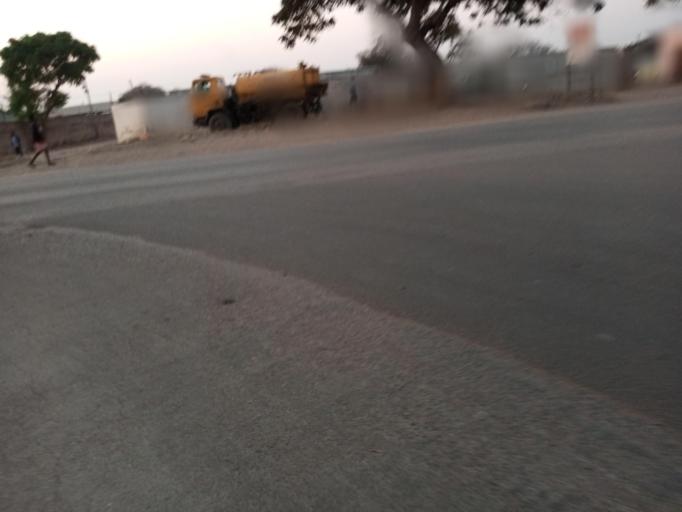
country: ZM
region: Lusaka
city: Lusaka
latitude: -15.3989
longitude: 28.2942
